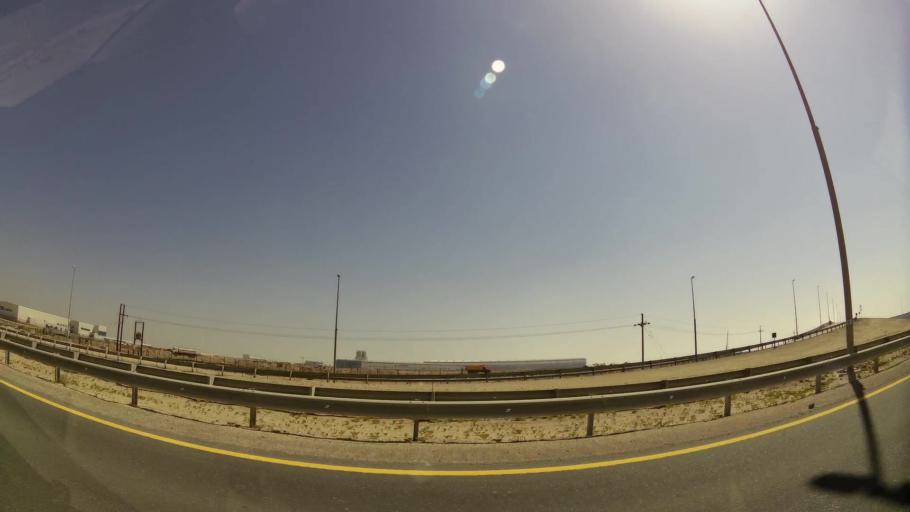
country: AE
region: Dubai
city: Dubai
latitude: 24.9213
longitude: 55.1010
